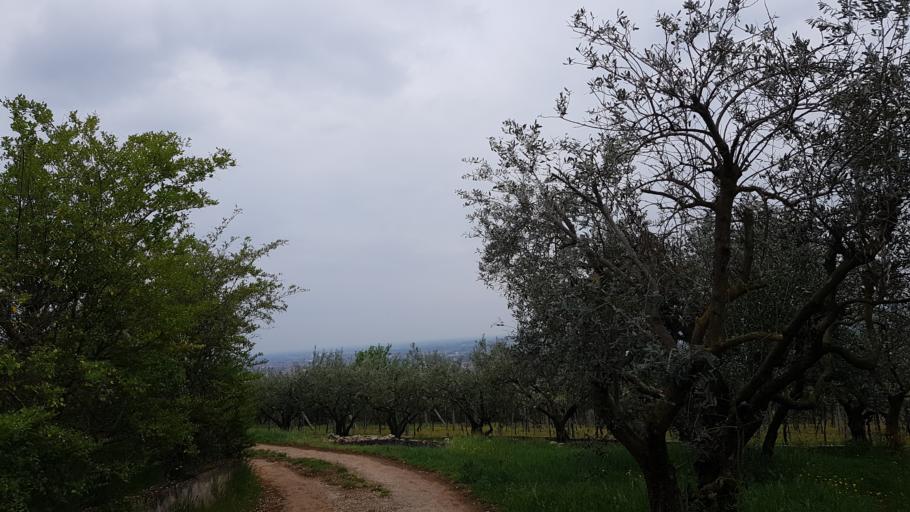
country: IT
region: Veneto
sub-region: Provincia di Verona
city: Parona
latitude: 45.4758
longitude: 10.9680
